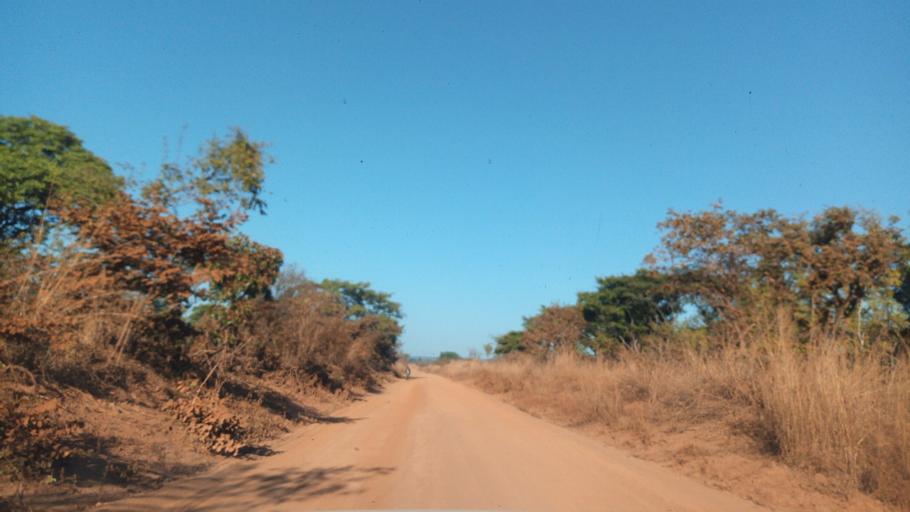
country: ZM
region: Luapula
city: Mwense
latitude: -10.5088
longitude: 28.4707
